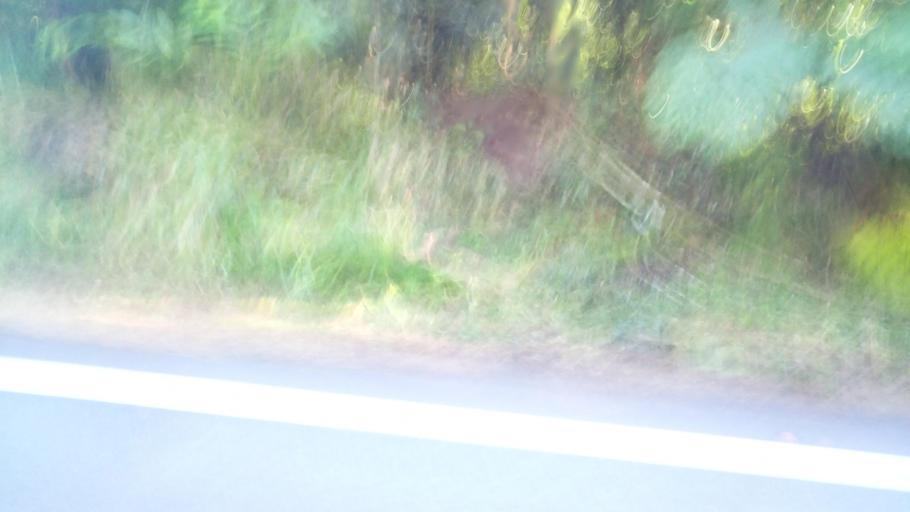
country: AU
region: Queensland
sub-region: Tablelands
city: Ravenshoe
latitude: -17.5950
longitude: 145.7450
